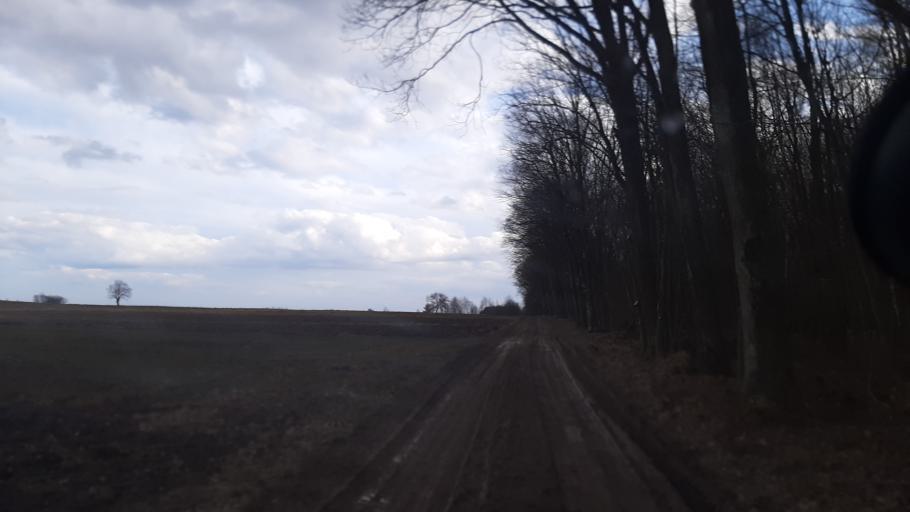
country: PL
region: Lublin Voivodeship
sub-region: Powiat lubelski
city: Jastkow
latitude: 51.3746
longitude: 22.4144
